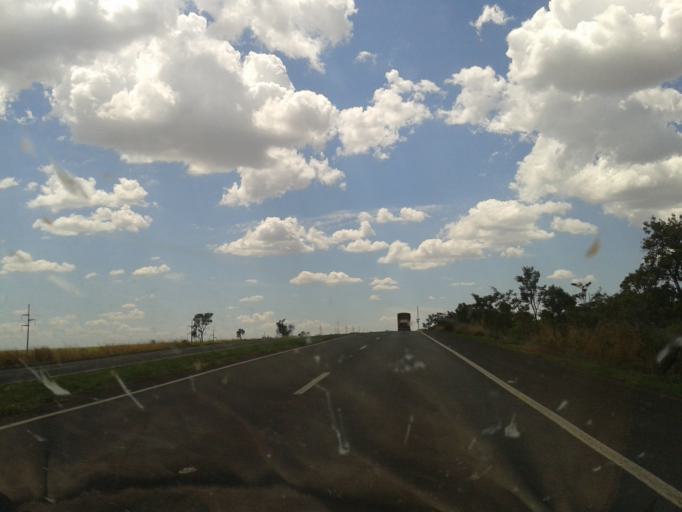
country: BR
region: Minas Gerais
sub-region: Uberlandia
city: Uberlandia
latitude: -19.1154
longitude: -48.1769
